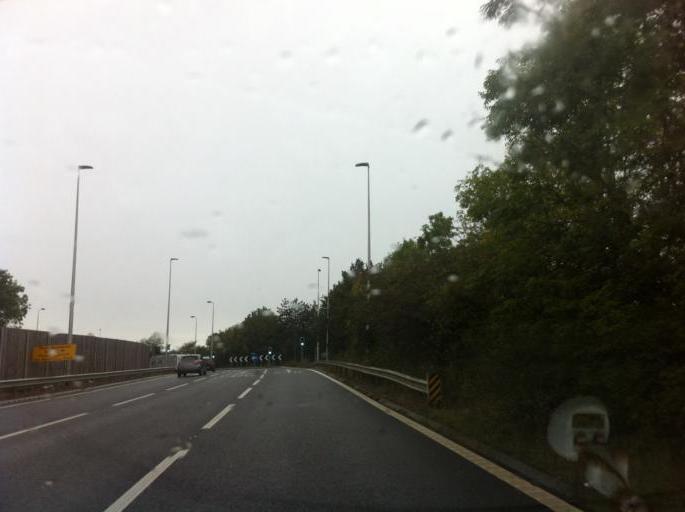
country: GB
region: England
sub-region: Peterborough
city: Newborough
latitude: 52.6038
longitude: -0.2282
